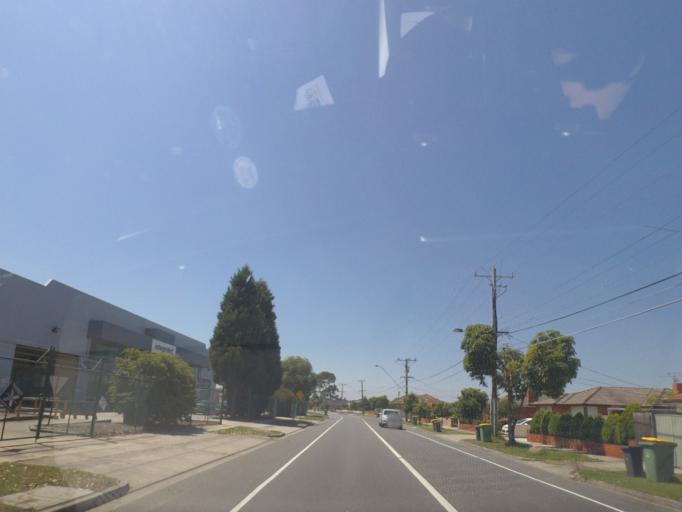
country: AU
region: Victoria
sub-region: Darebin
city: Reservoir
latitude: -37.7084
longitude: 144.9900
